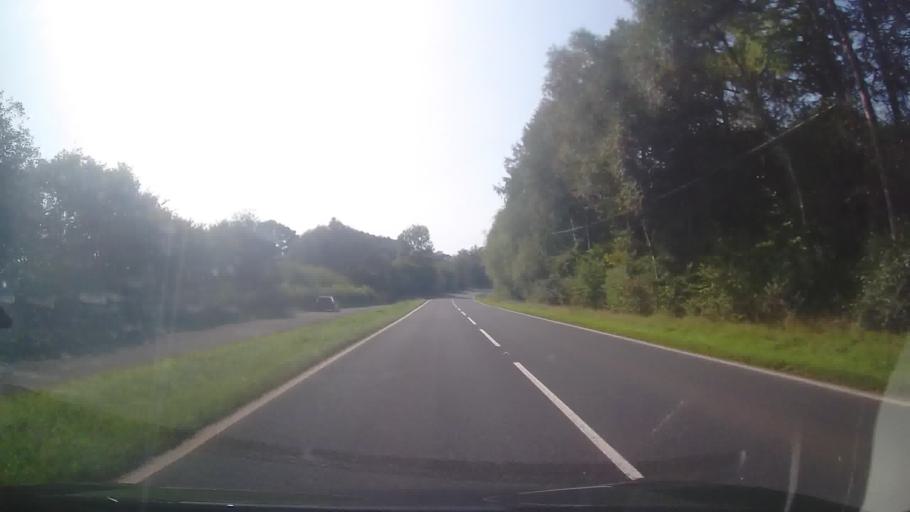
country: GB
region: Wales
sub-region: Sir Powys
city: Rhayader
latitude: 52.1249
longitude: -3.6160
